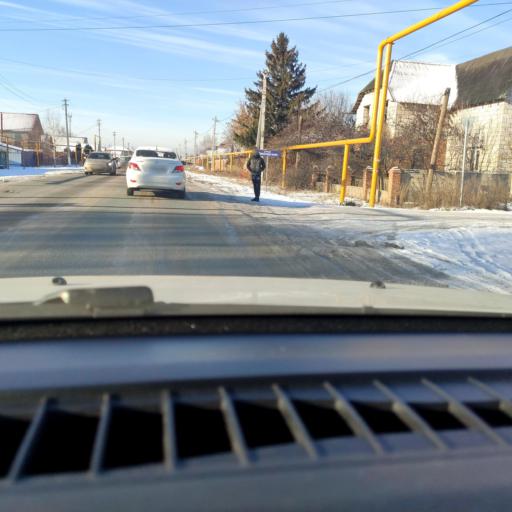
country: RU
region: Samara
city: Podstepki
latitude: 53.5163
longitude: 49.1372
